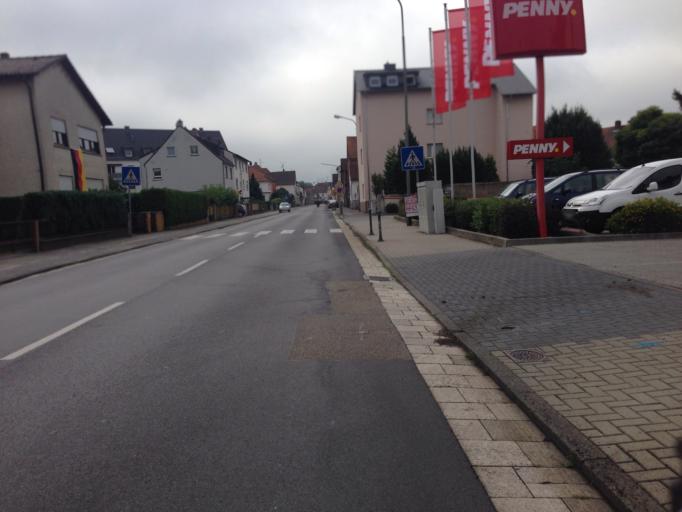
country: DE
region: Hesse
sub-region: Regierungsbezirk Darmstadt
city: Hanau am Main
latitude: 50.1031
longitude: 8.9215
